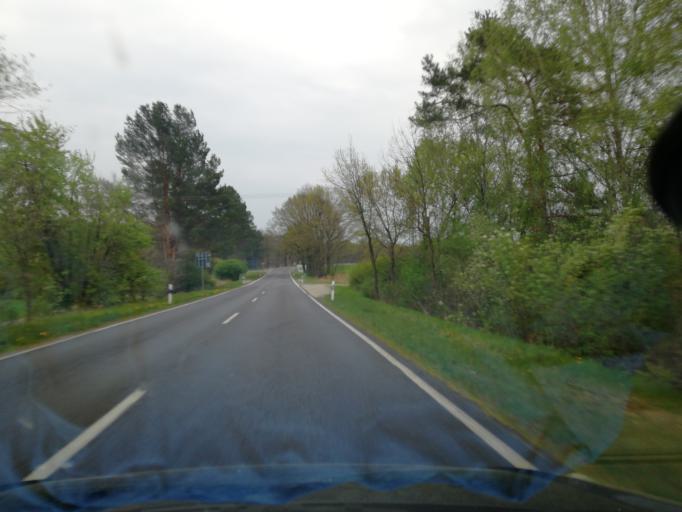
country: DE
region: Brandenburg
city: Calau
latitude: 51.7838
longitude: 13.8798
